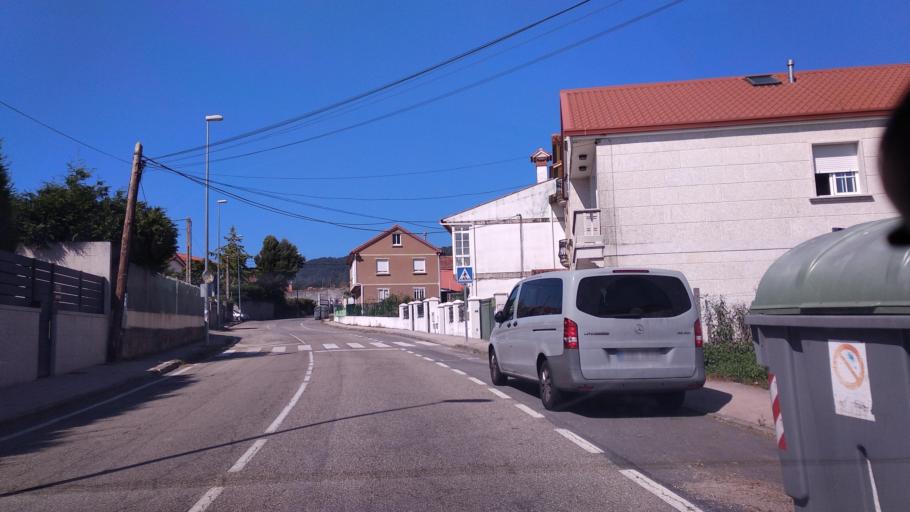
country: ES
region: Galicia
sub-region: Provincia de Pontevedra
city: Cangas
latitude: 42.2693
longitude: -8.7677
